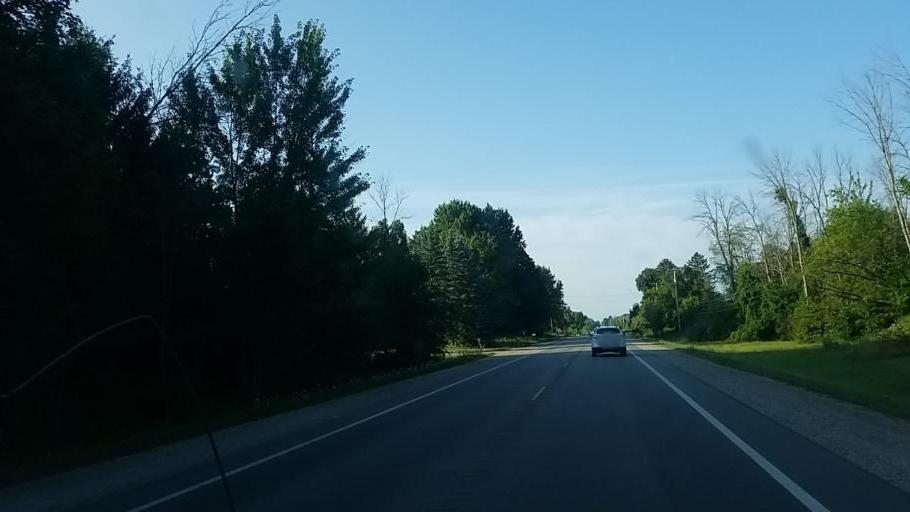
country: US
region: Michigan
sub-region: Montcalm County
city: Stanton
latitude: 43.2292
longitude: -85.0735
